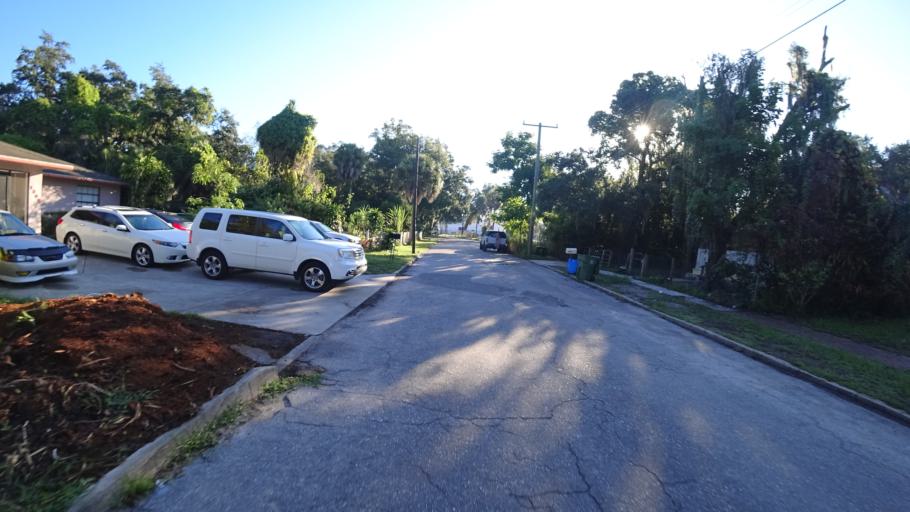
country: US
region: Florida
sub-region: Manatee County
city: Bradenton
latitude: 27.4963
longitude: -82.5495
